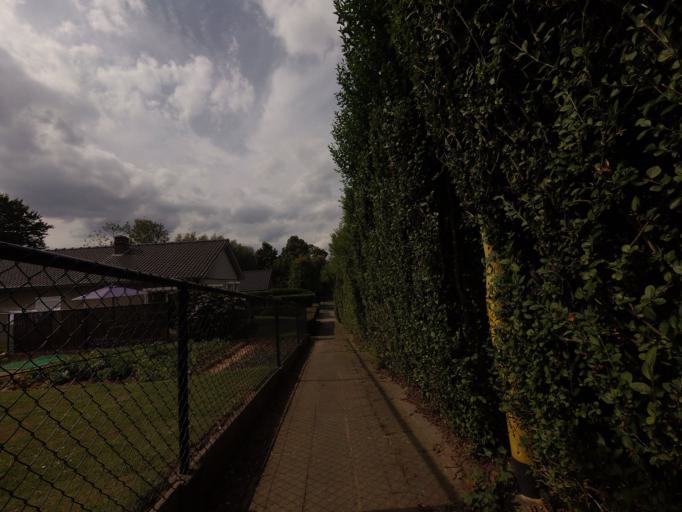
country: BE
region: Flanders
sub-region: Provincie Vlaams-Brabant
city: Grimbergen
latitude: 50.9233
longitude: 4.3684
